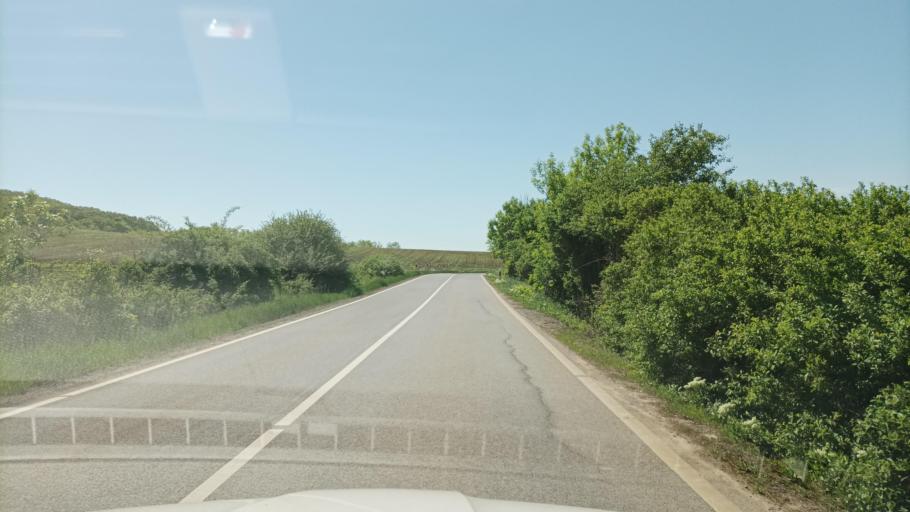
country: HU
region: Pest
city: Acsa
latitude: 47.7623
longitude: 19.3715
